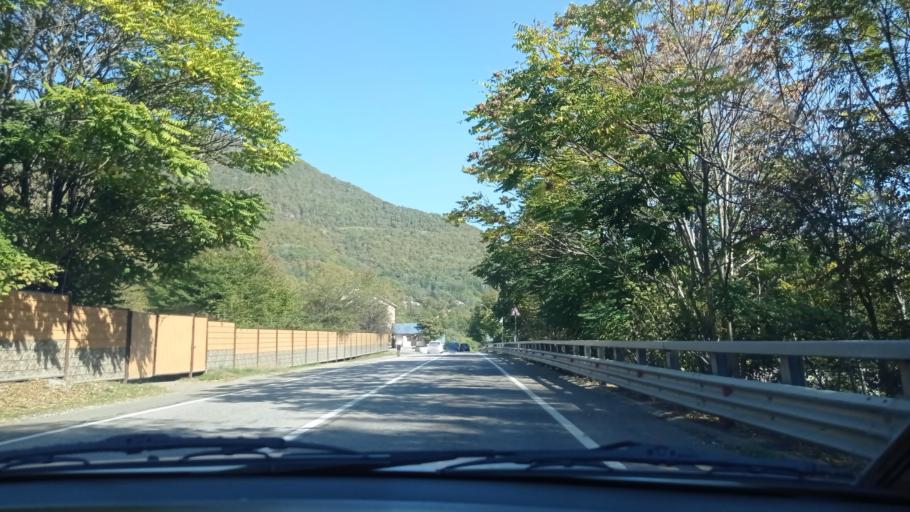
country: RU
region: Krasnodarskiy
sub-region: Sochi City
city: Krasnaya Polyana
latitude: 43.6825
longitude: 40.2232
